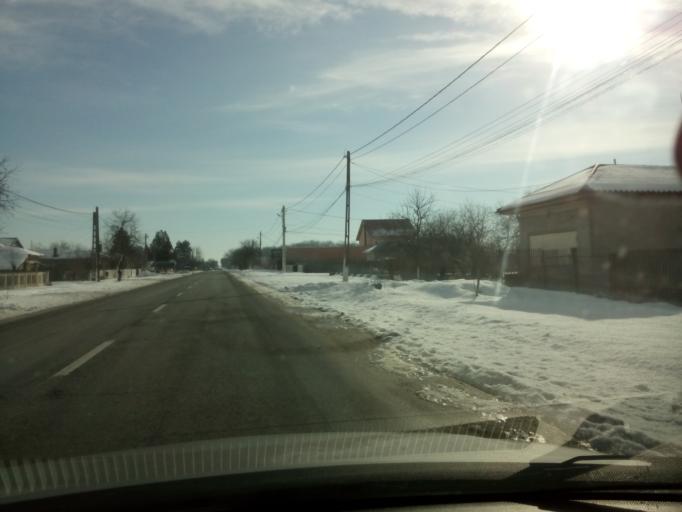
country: RO
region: Calarasi
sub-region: Comuna Frumusani
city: Frumusani
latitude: 44.2853
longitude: 26.3262
